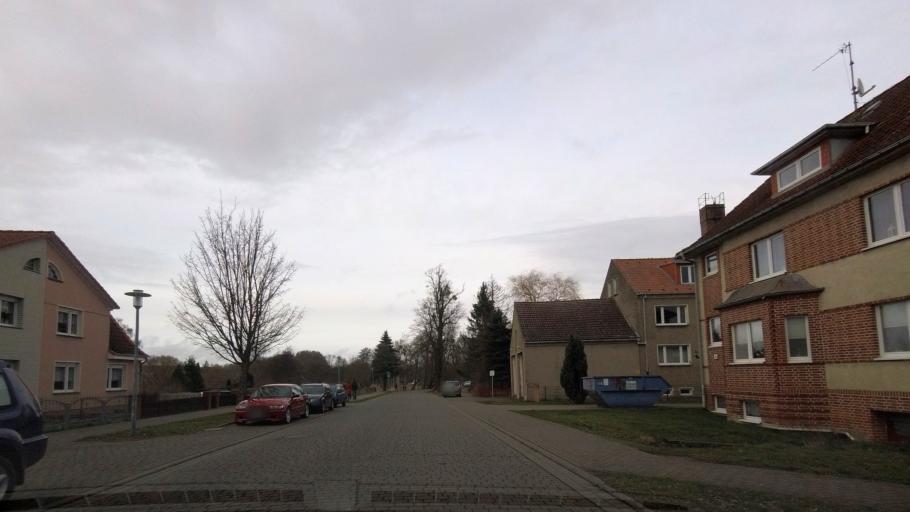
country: DE
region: Mecklenburg-Vorpommern
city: Robel
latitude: 53.3761
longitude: 12.6027
